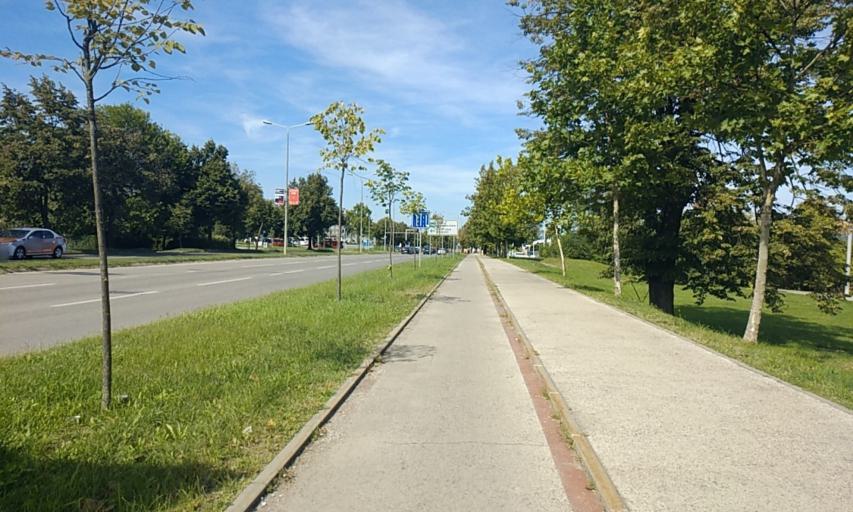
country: BA
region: Republika Srpska
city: Banja Luka
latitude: 44.7825
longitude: 17.2062
